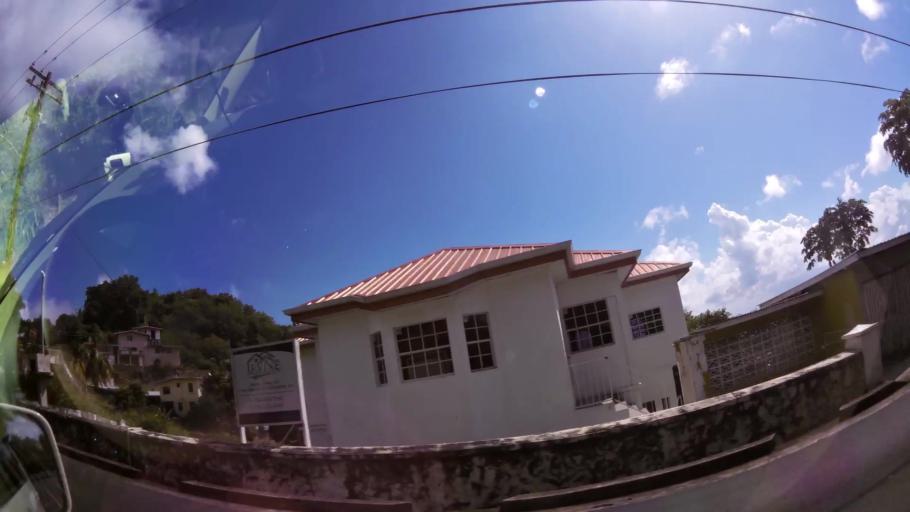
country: VC
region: Saint George
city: Kingstown
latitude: 13.1387
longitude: -61.2070
